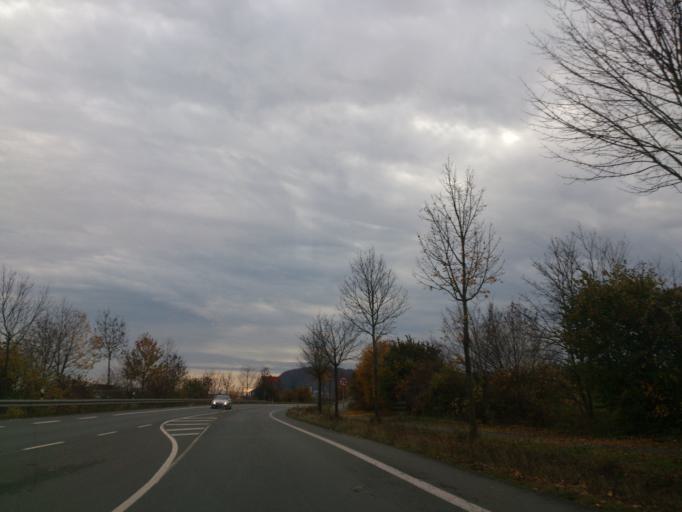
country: DE
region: North Rhine-Westphalia
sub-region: Regierungsbezirk Detmold
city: Hoexter
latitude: 51.7905
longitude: 9.3936
